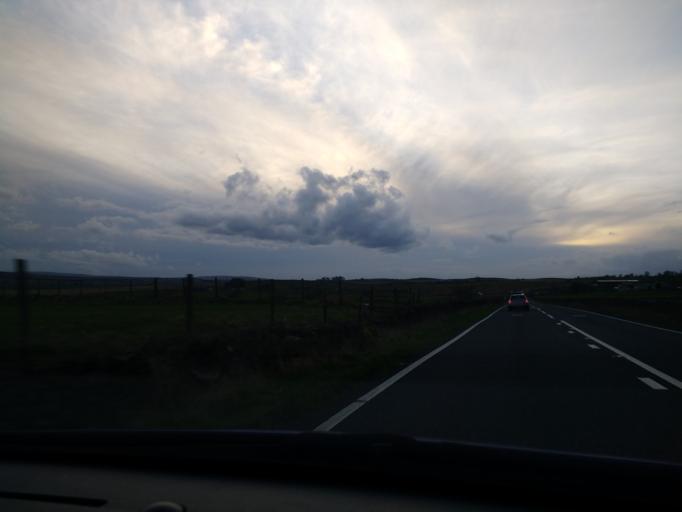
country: GB
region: England
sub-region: North Yorkshire
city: Ingleton
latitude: 54.1233
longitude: -2.4134
